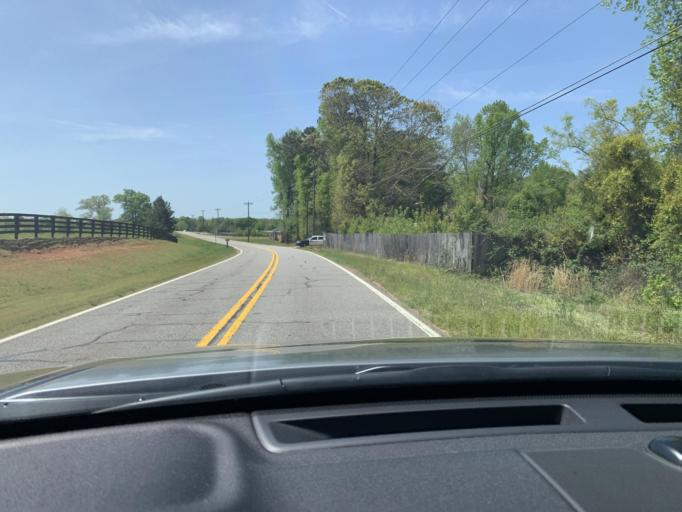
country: US
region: Georgia
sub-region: Barrow County
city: Statham
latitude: 33.9066
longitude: -83.5978
